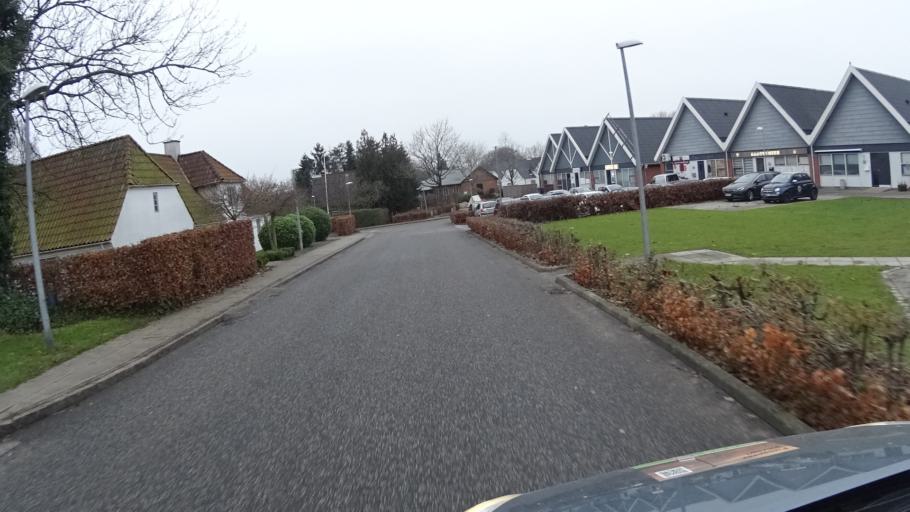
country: DK
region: South Denmark
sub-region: Vejle Kommune
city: Vejle
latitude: 55.7183
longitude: 9.6090
